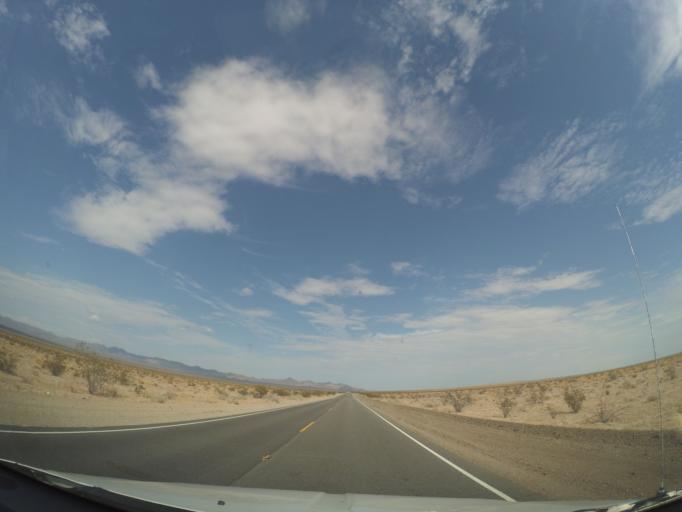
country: US
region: California
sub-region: Riverside County
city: Mesa Verde
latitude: 34.1016
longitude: -114.9865
